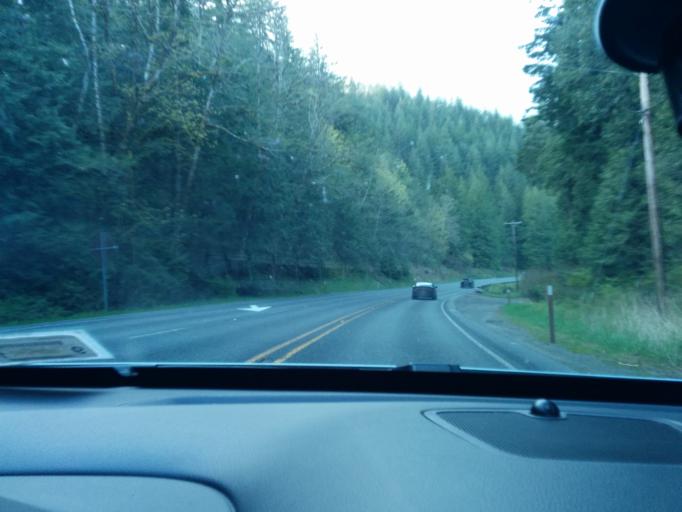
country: US
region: Washington
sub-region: Snohomish County
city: Gold Bar
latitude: 47.8261
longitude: -121.6191
